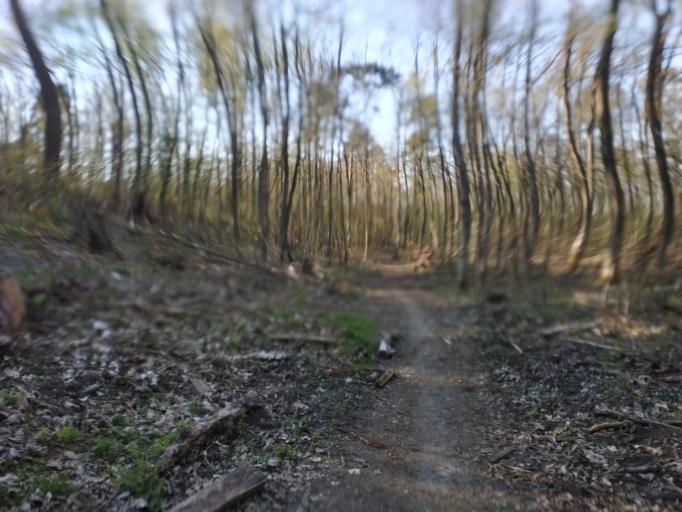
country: DE
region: Brandenburg
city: Petershagen
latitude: 52.5646
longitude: 13.8284
